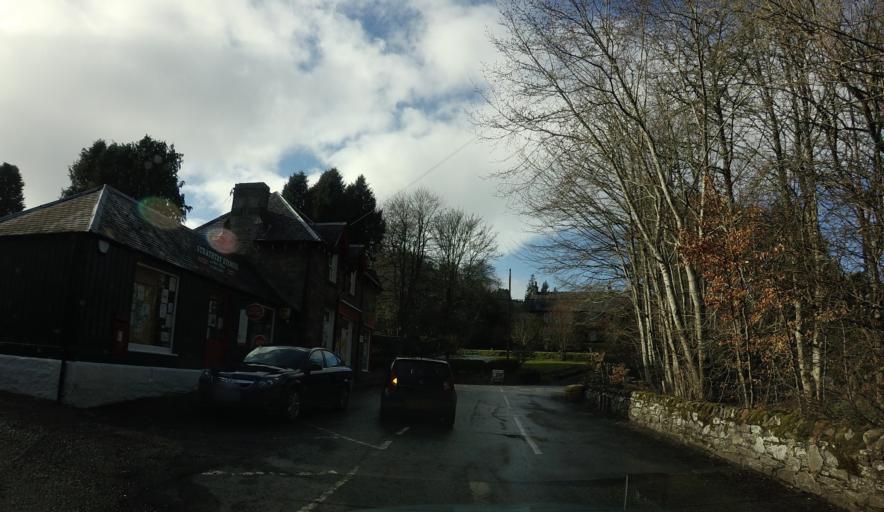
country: GB
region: Scotland
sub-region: Perth and Kinross
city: Pitlochry
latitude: 56.6598
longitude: -3.7777
